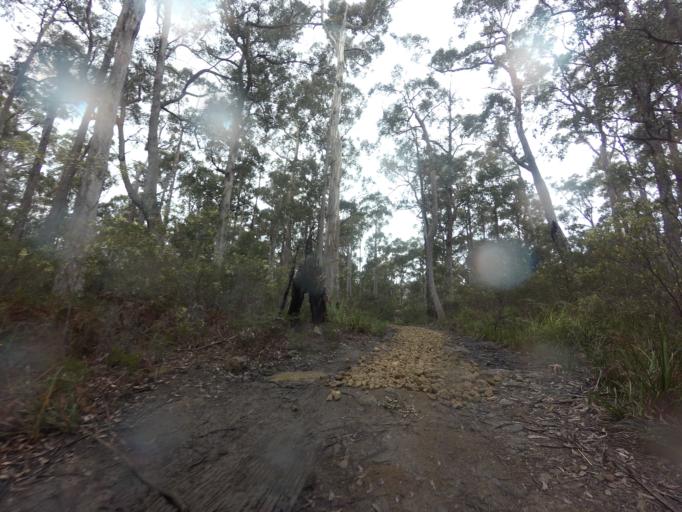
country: AU
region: Tasmania
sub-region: Huon Valley
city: Geeveston
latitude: -43.4642
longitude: 146.9269
